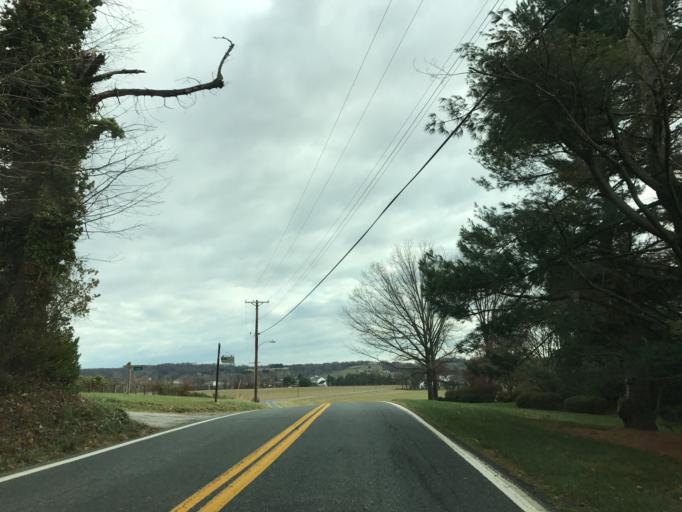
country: US
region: Maryland
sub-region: Baltimore County
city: Perry Hall
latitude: 39.4859
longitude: -76.5007
